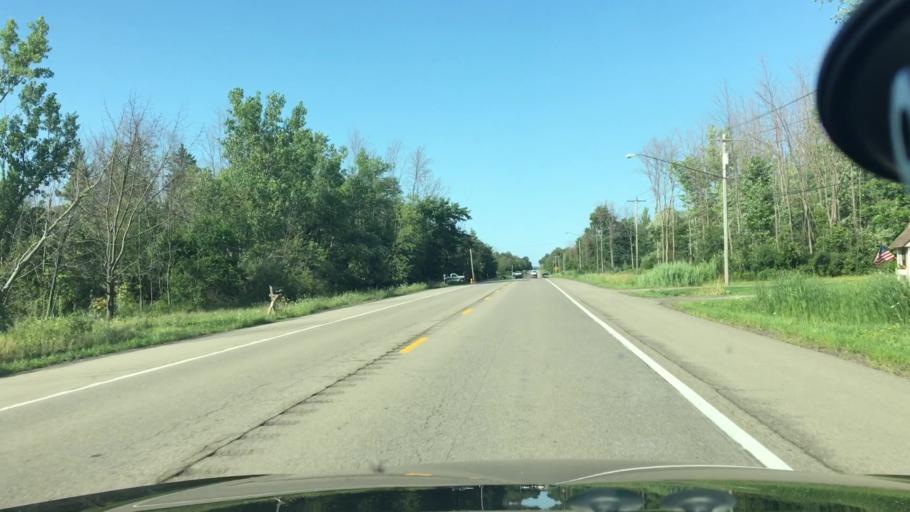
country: US
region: New York
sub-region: Erie County
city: Angola
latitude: 42.6564
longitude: -78.9767
